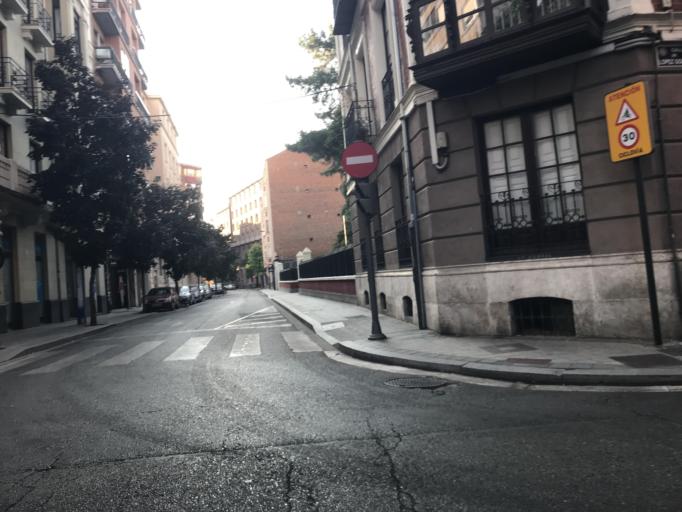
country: ES
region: Castille and Leon
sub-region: Provincia de Valladolid
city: Valladolid
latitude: 41.6501
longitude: -4.7240
